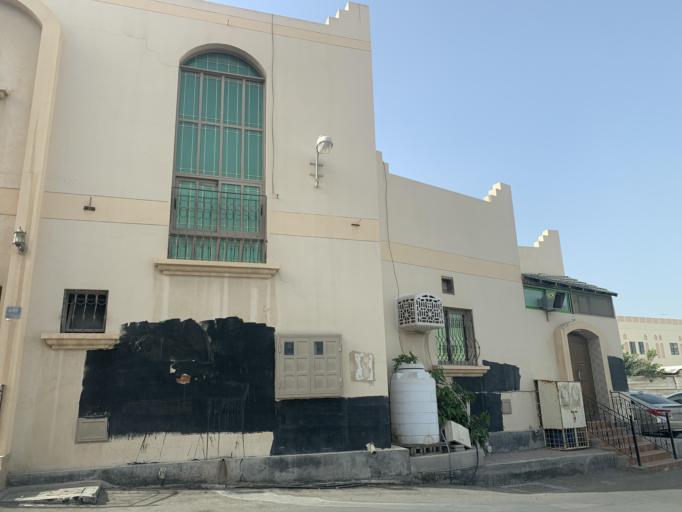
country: BH
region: Northern
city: Madinat `Isa
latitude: 26.1622
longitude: 50.5171
